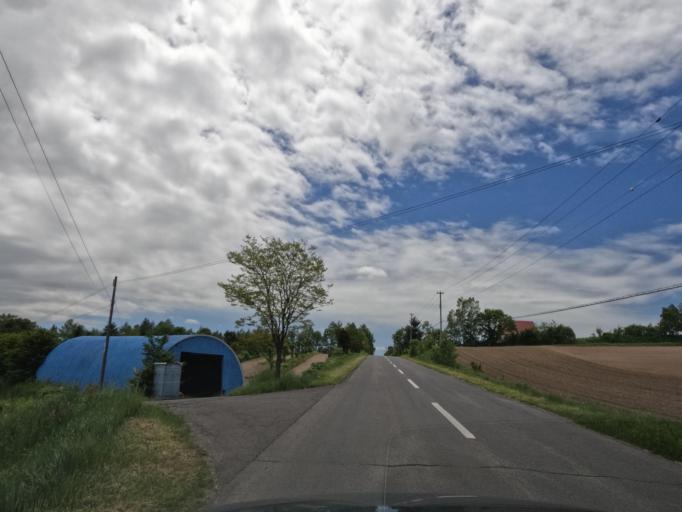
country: JP
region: Hokkaido
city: Shimo-furano
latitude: 43.5233
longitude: 142.4330
